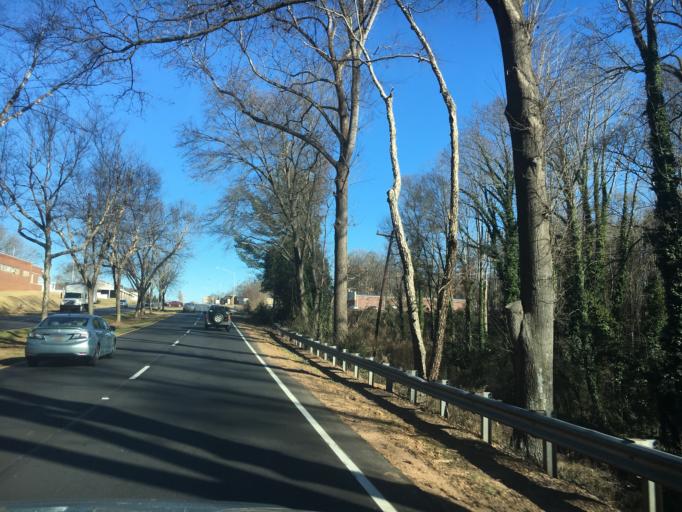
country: US
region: South Carolina
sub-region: Spartanburg County
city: Saxon
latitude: 34.9403
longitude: -81.9571
